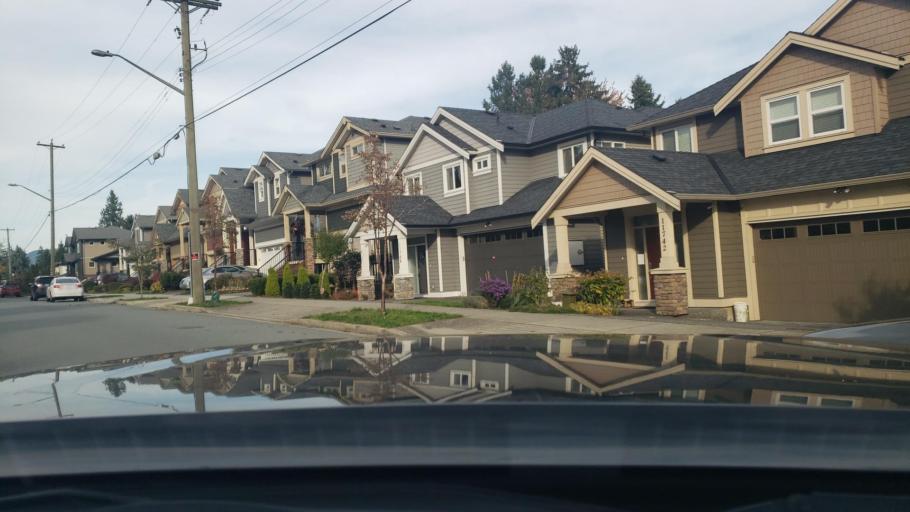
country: CA
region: British Columbia
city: Maple Ridge
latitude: 49.2155
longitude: -122.5681
